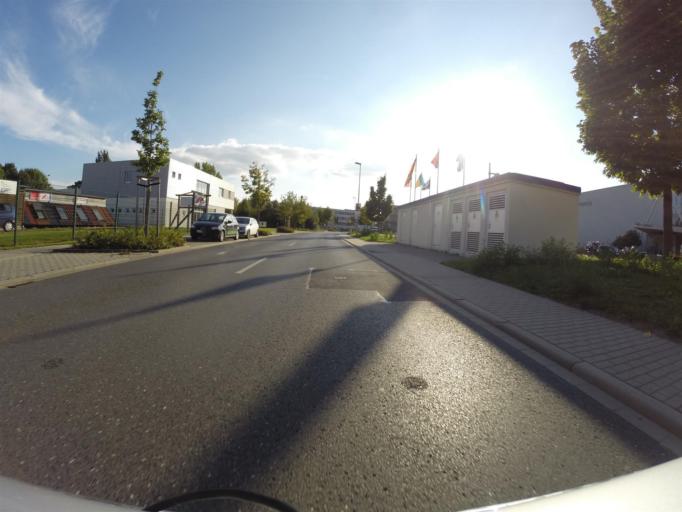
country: DE
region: Thuringia
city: Jena
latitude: 50.9445
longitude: 11.6070
